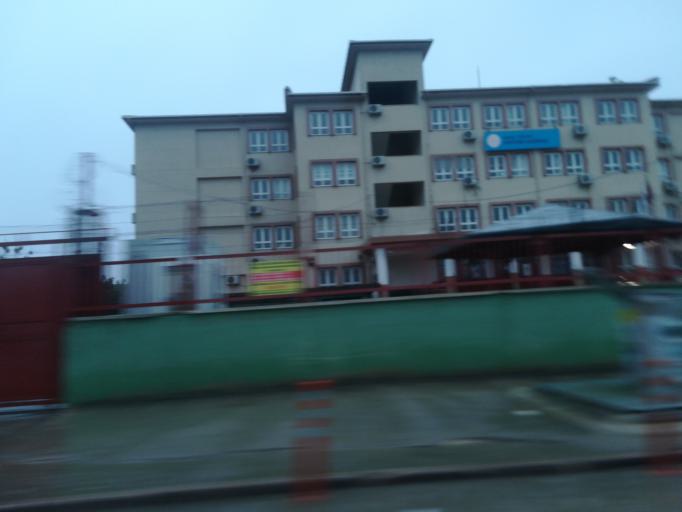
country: TR
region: Adana
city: Seyhan
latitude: 37.0060
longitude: 35.2801
